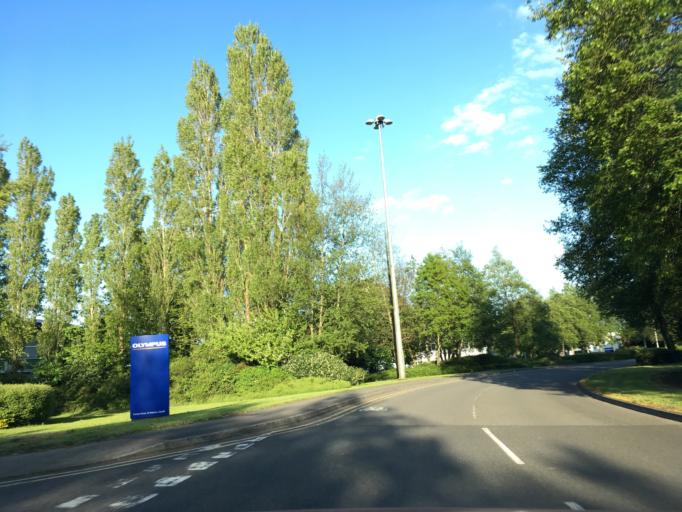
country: GB
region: Wales
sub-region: Newport
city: Marshfield
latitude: 51.5290
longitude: -3.0827
